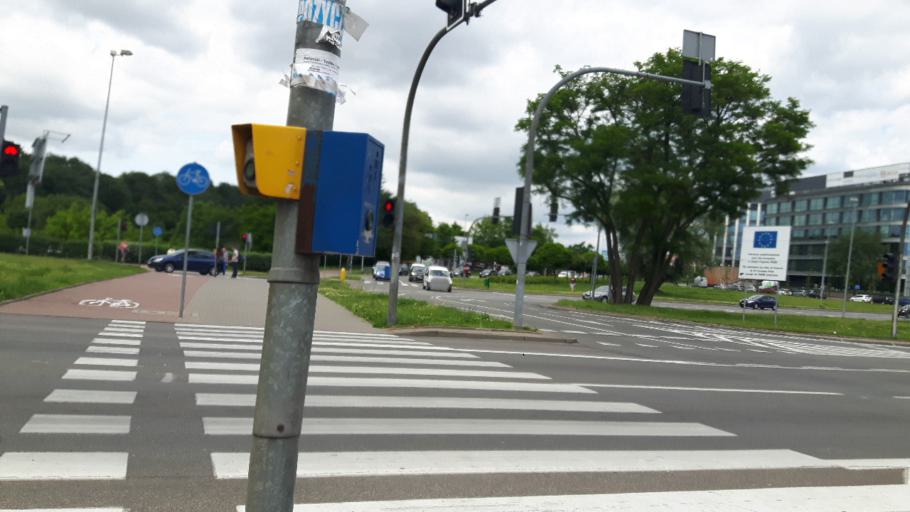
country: PL
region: West Pomeranian Voivodeship
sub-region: Szczecin
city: Szczecin
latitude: 53.4160
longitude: 14.5316
